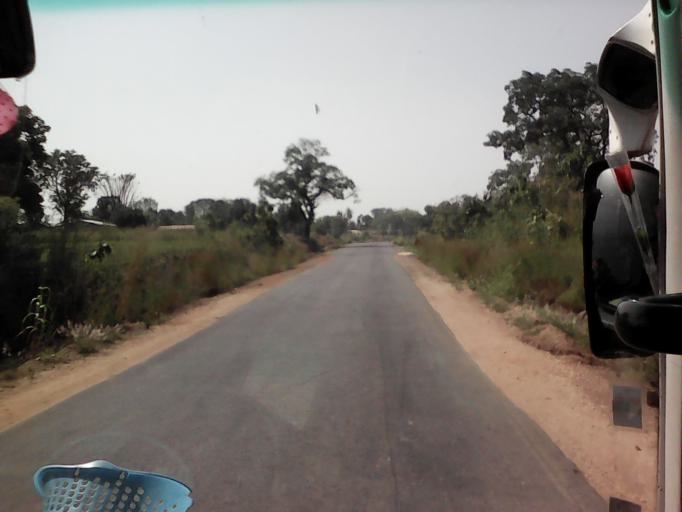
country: TG
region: Centrale
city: Sotouboua
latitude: 8.6807
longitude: 1.0232
